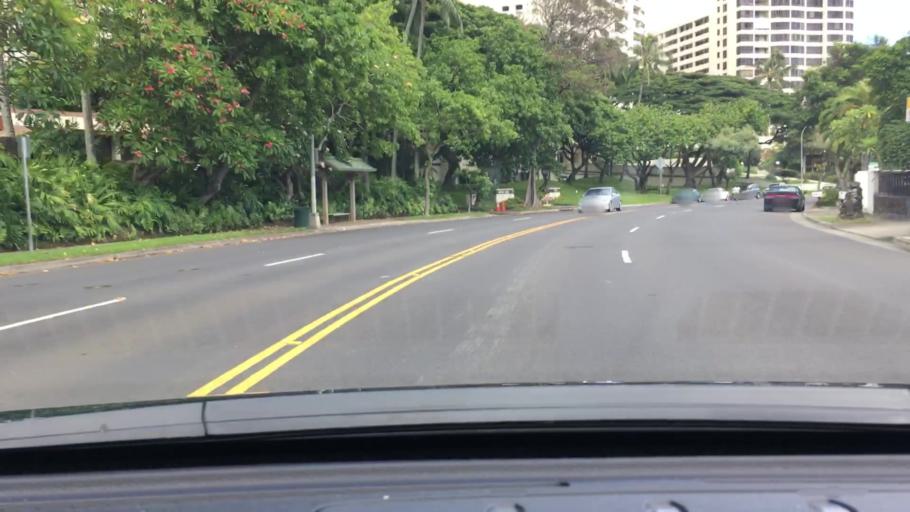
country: US
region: Hawaii
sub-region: Honolulu County
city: Waimanalo Beach
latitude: 21.2935
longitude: -157.7082
